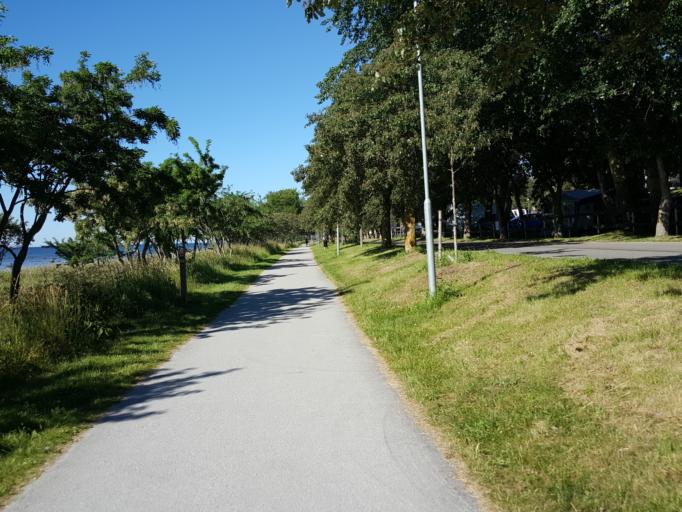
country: SE
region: Gotland
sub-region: Gotland
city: Visby
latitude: 57.6554
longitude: 18.3073
